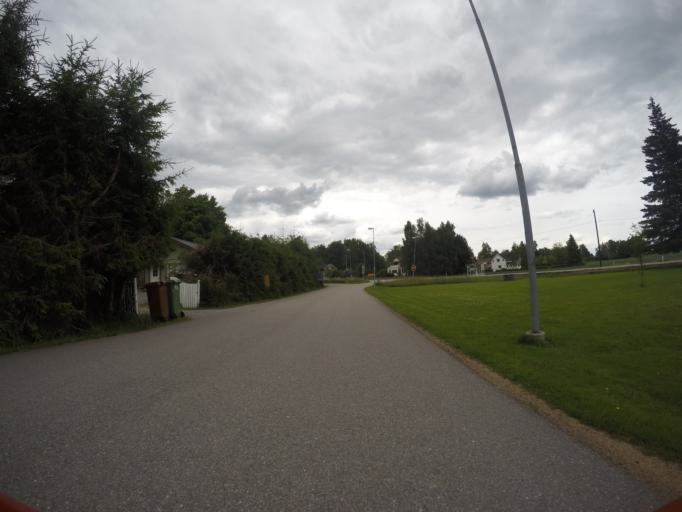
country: SE
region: Vaestra Goetaland
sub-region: Vanersborgs Kommun
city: Vargon
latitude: 58.2505
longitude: 12.4173
